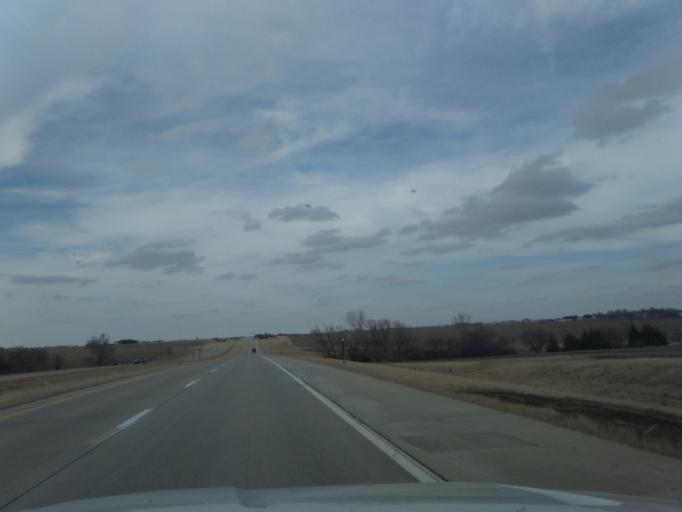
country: US
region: Nebraska
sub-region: Gage County
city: Beatrice
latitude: 40.3648
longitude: -96.7422
